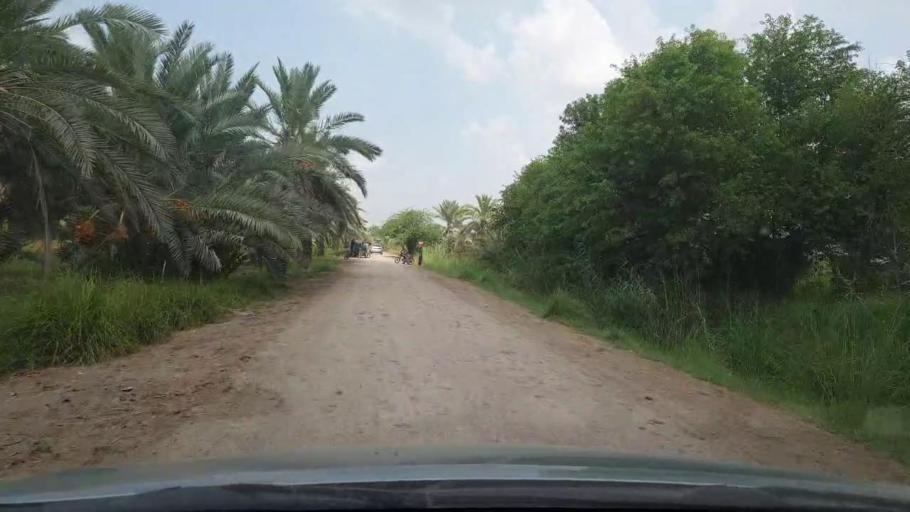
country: PK
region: Sindh
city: Khairpur
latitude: 27.4665
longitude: 68.7703
